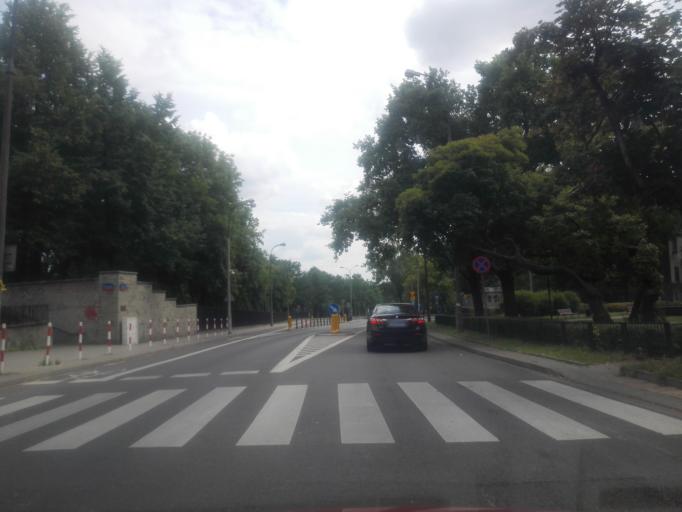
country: PL
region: Masovian Voivodeship
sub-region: Warszawa
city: Srodmiescie
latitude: 52.2121
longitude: 21.0236
